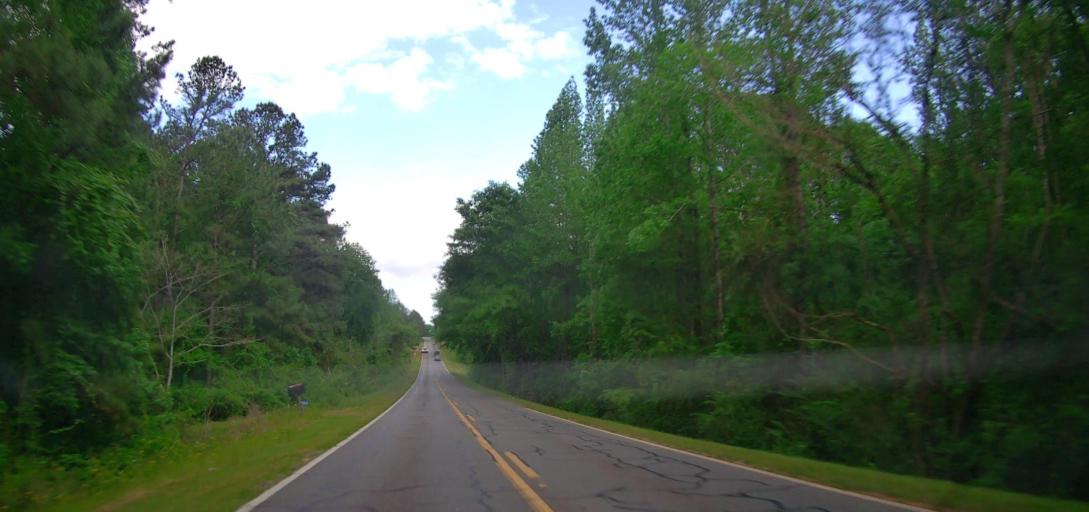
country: US
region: Georgia
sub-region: Baldwin County
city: Hardwick
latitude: 33.0630
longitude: -83.1475
